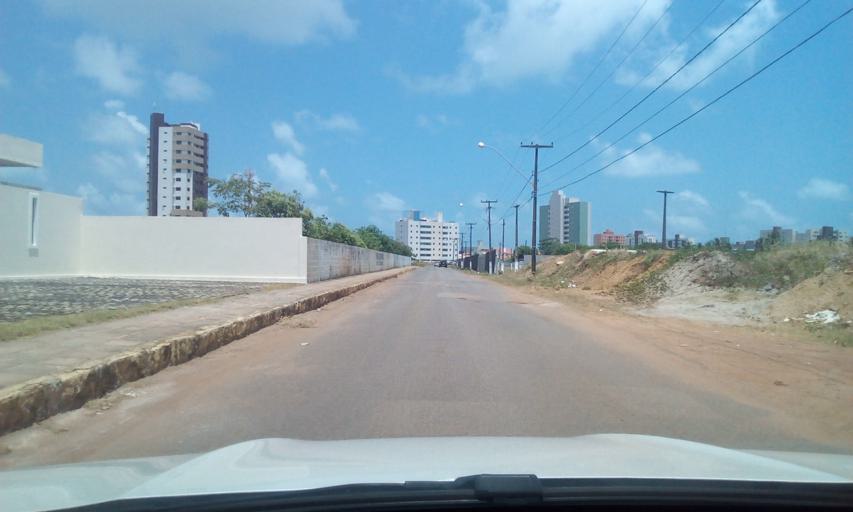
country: BR
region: Paraiba
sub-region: Cabedelo
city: Cabedelo
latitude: -7.0317
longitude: -34.8387
